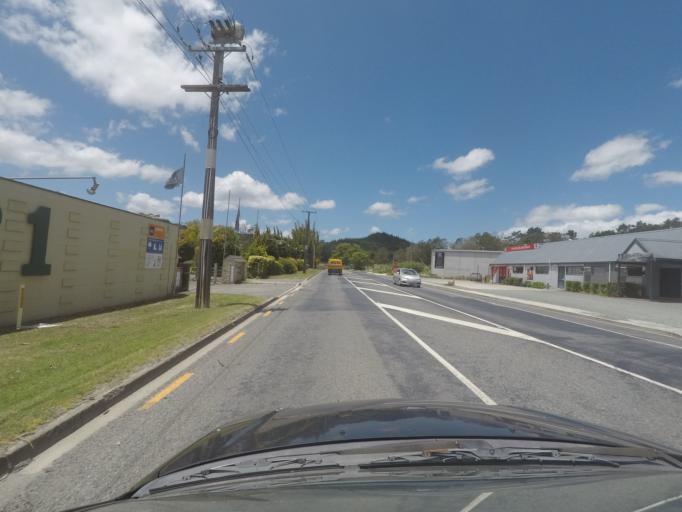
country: NZ
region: Northland
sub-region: Whangarei
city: Whangarei
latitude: -35.7521
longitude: 174.3174
